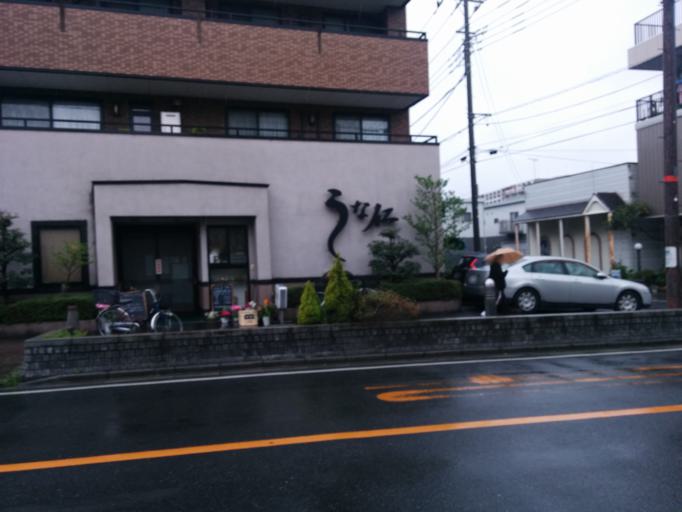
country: JP
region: Saitama
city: Shimotoda
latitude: 35.8182
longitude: 139.6772
